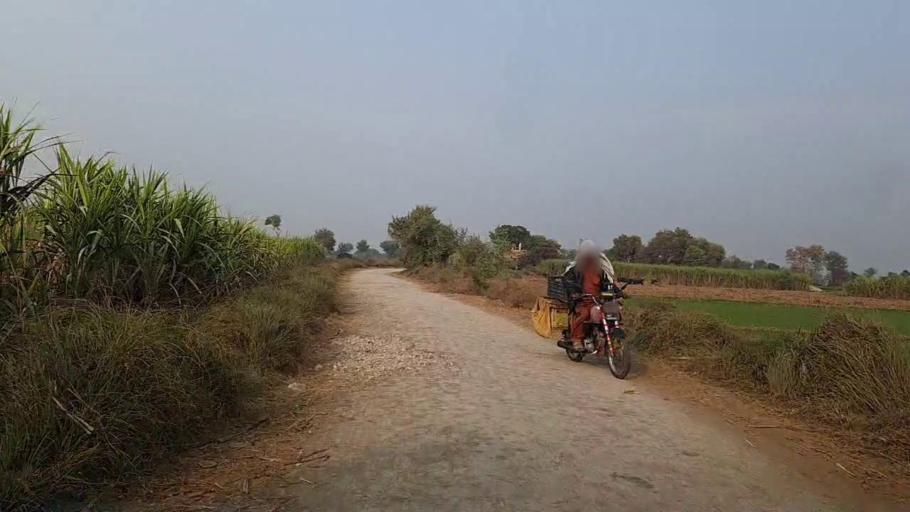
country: PK
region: Sindh
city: Setharja Old
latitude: 27.0946
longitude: 68.5006
